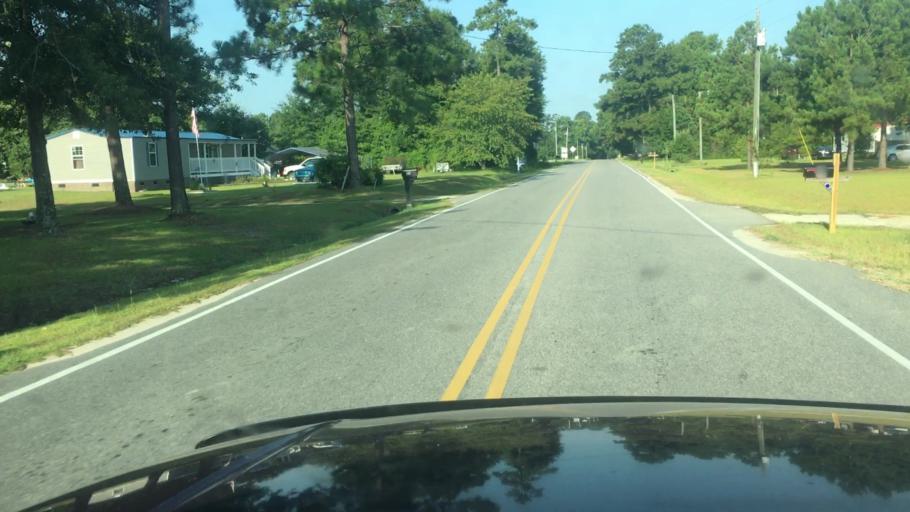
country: US
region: North Carolina
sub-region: Robeson County
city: Saint Pauls
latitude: 34.8354
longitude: -78.8942
